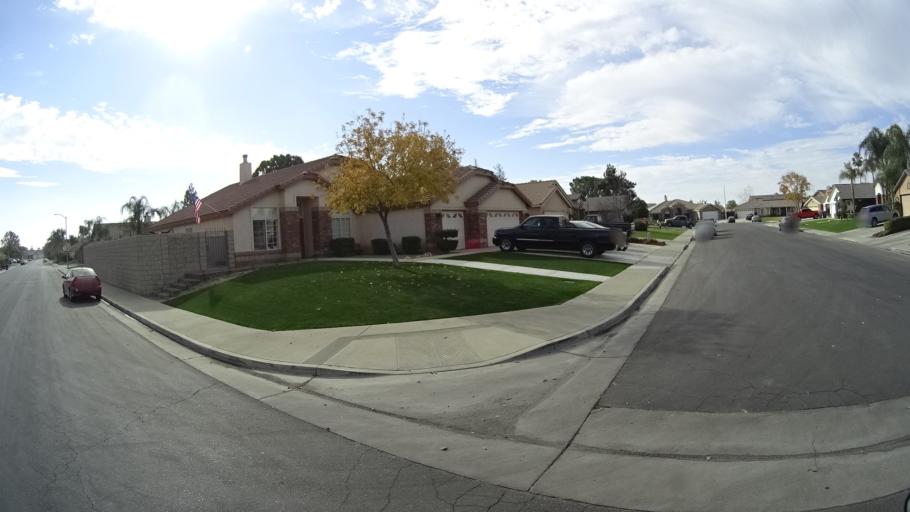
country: US
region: California
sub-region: Kern County
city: Greenacres
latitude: 35.4026
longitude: -119.1235
